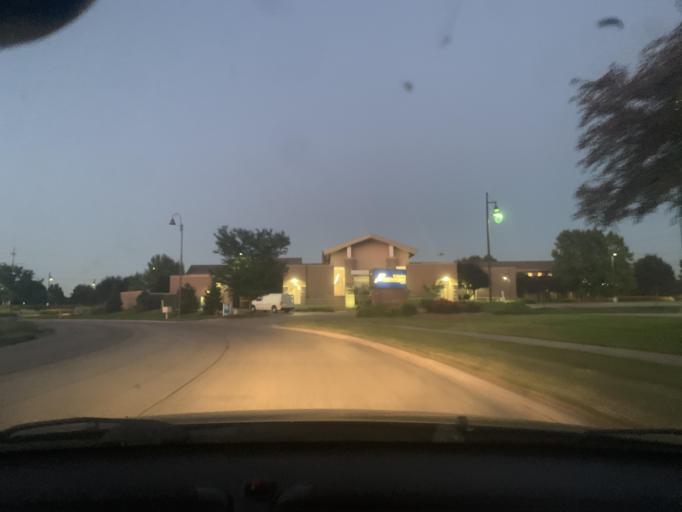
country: US
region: Nebraska
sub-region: Sarpy County
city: Papillion
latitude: 41.1770
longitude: -96.0639
